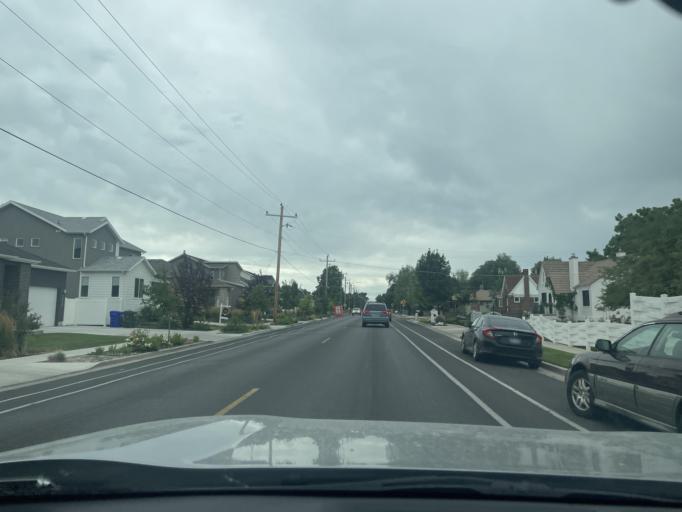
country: US
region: Utah
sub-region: Salt Lake County
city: Millcreek
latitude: 40.6967
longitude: -111.8770
